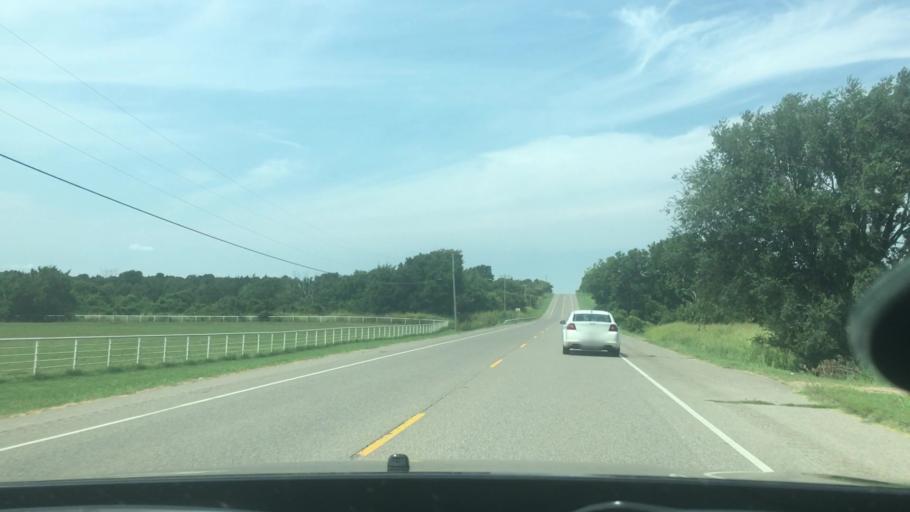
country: US
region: Oklahoma
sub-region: Pottawatomie County
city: Shawnee
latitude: 35.3331
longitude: -96.8295
